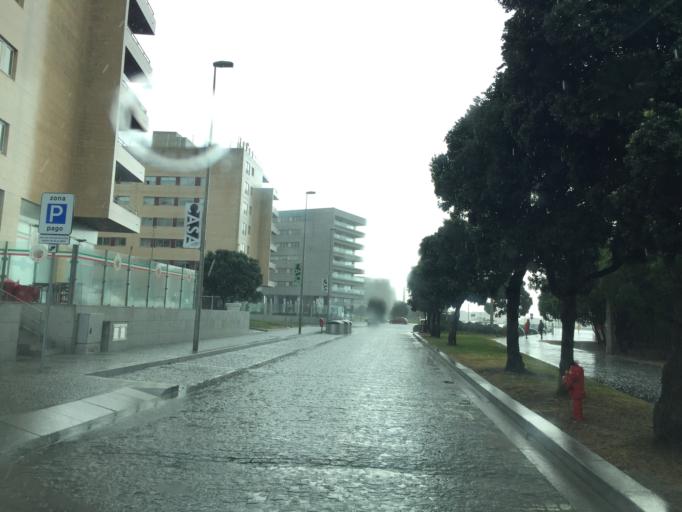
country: PT
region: Porto
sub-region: Matosinhos
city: Matosinhos
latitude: 41.1806
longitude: -8.6942
